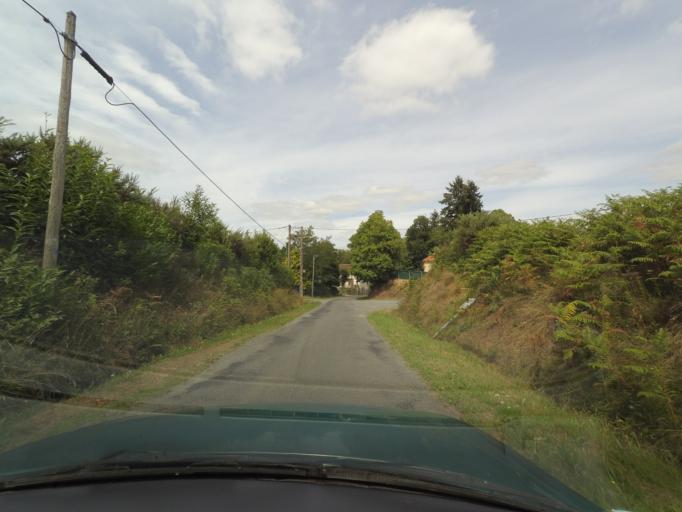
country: FR
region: Limousin
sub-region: Departement de la Haute-Vienne
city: Ladignac-le-Long
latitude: 45.6459
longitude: 1.1235
